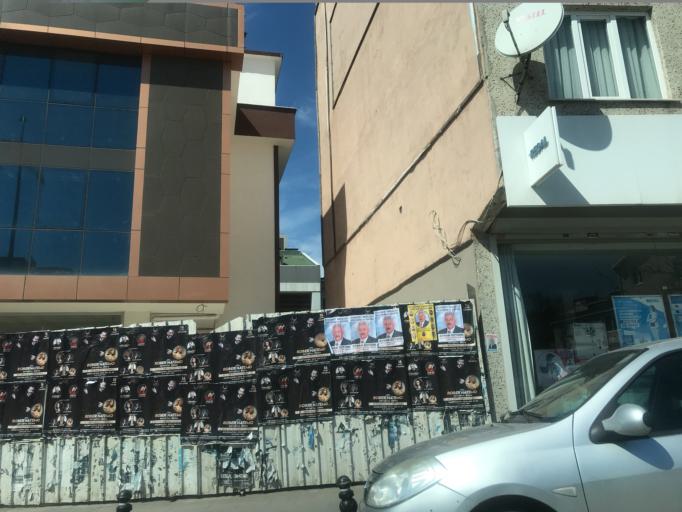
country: TR
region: Istanbul
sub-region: Atasehir
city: Atasehir
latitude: 40.9720
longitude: 29.1084
